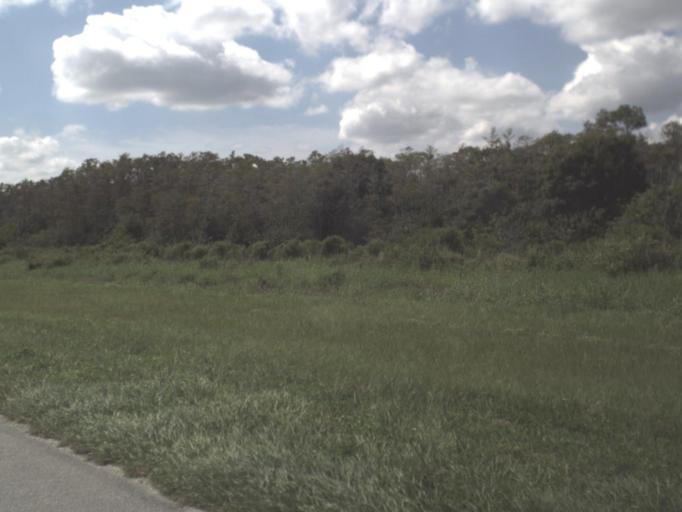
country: US
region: Florida
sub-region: Hendry County
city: Port LaBelle
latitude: 26.6569
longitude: -81.4362
